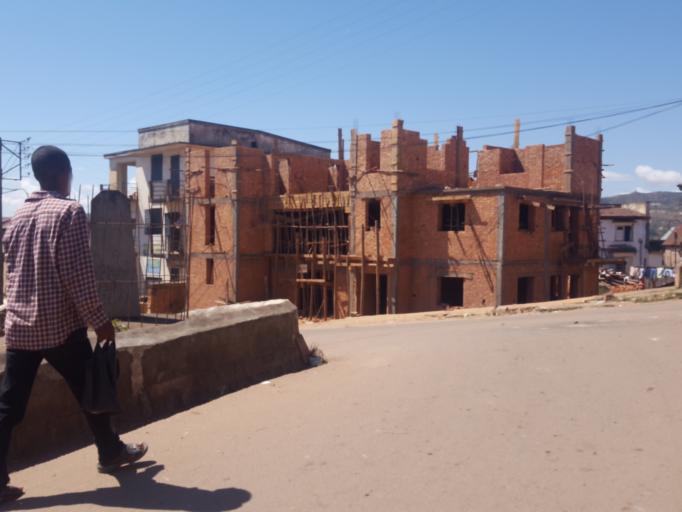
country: MG
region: Amoron'i Mania
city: Ambositra
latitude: -20.5316
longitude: 47.2459
